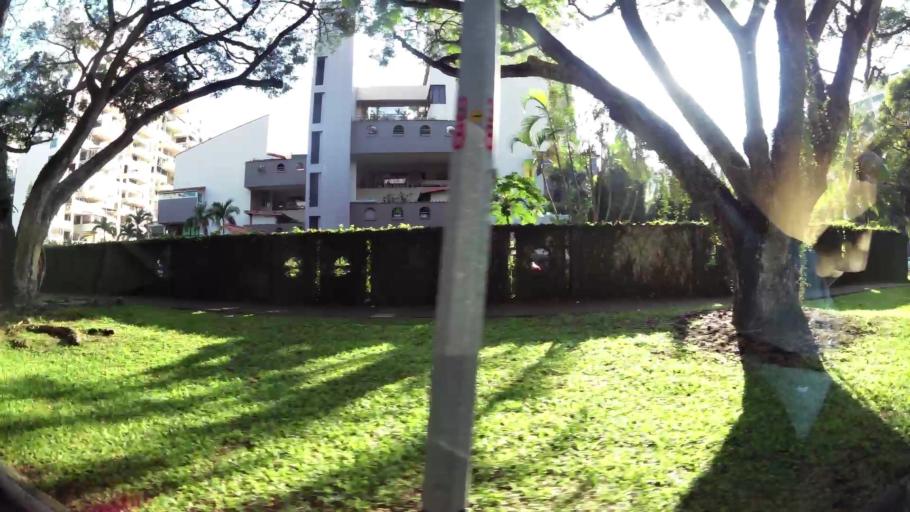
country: SG
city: Singapore
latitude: 1.3213
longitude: 103.9441
